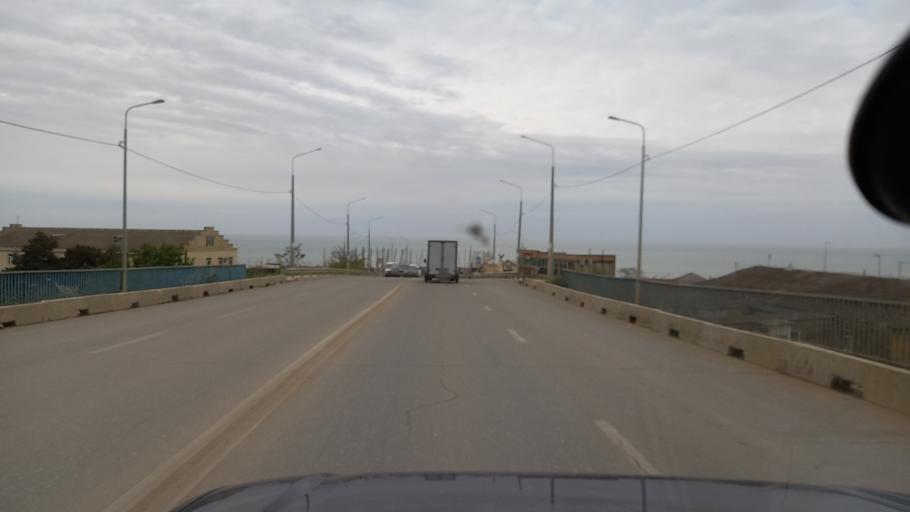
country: RU
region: Dagestan
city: Derbent
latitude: 42.0717
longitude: 48.2987
